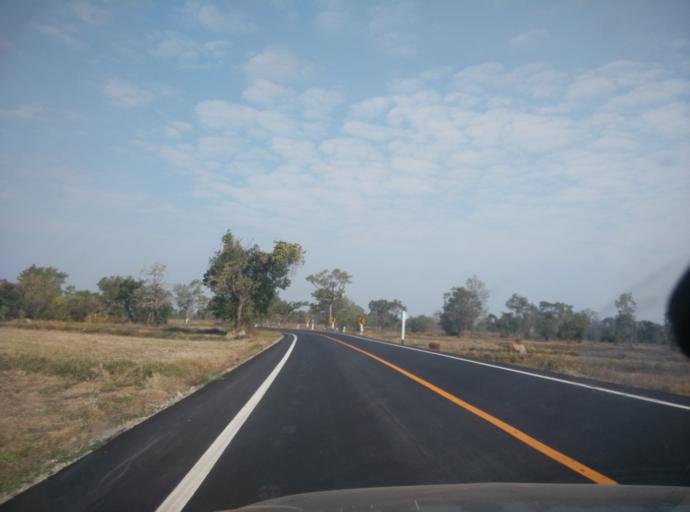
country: TH
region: Sisaket
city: Si Sa Ket
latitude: 15.1200
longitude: 104.2514
